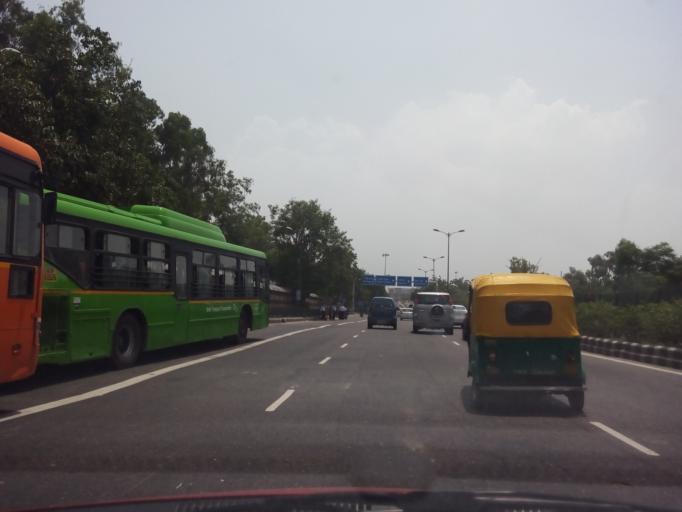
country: IN
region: NCT
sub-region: North West Delhi
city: Pitampura
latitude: 28.6585
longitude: 77.1285
